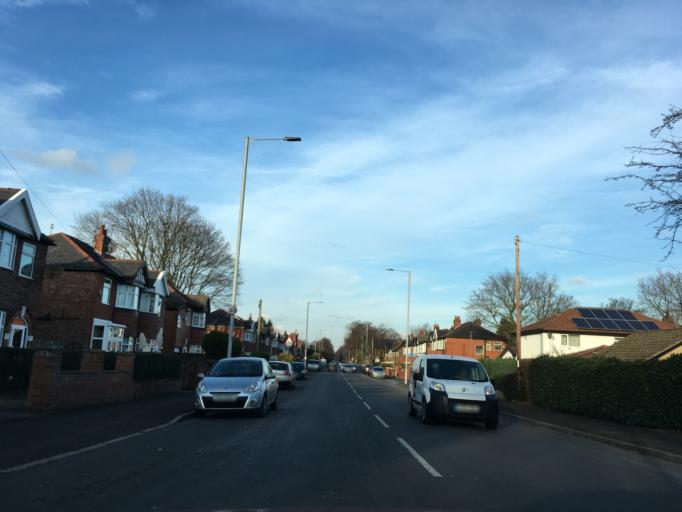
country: GB
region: England
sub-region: Manchester
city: Chorlton cum Hardy
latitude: 53.4412
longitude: -2.2516
